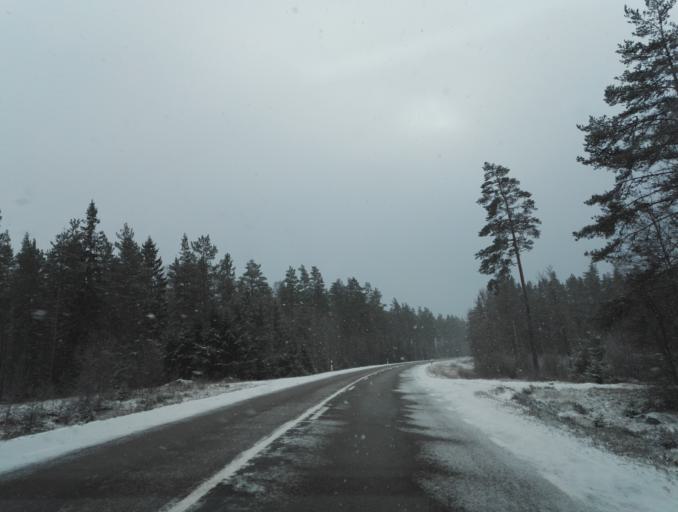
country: SE
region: Kronoberg
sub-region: Uppvidinge Kommun
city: Lenhovda
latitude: 56.9145
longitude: 15.3668
